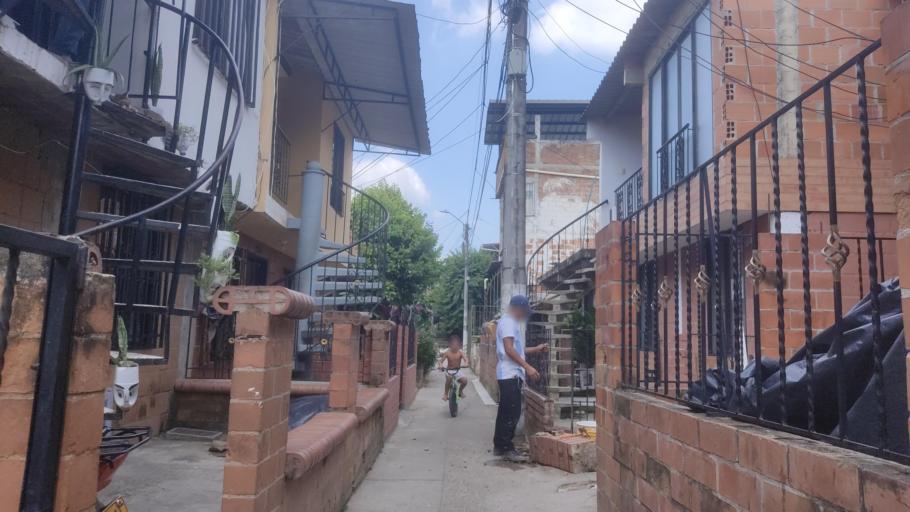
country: CO
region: Valle del Cauca
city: Jamundi
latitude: 3.2511
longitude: -76.5427
